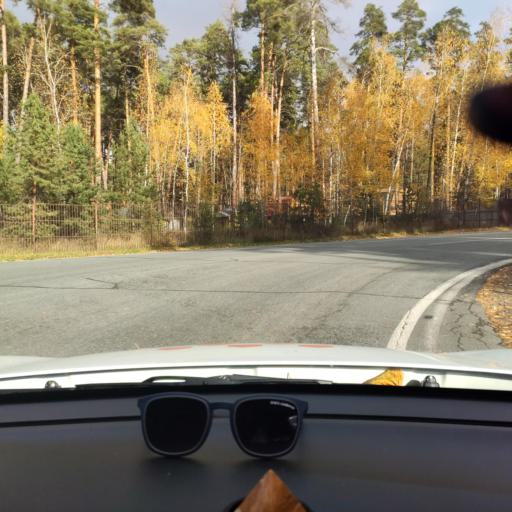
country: RU
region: Tatarstan
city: Verkhniy Uslon
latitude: 55.6399
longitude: 49.0231
